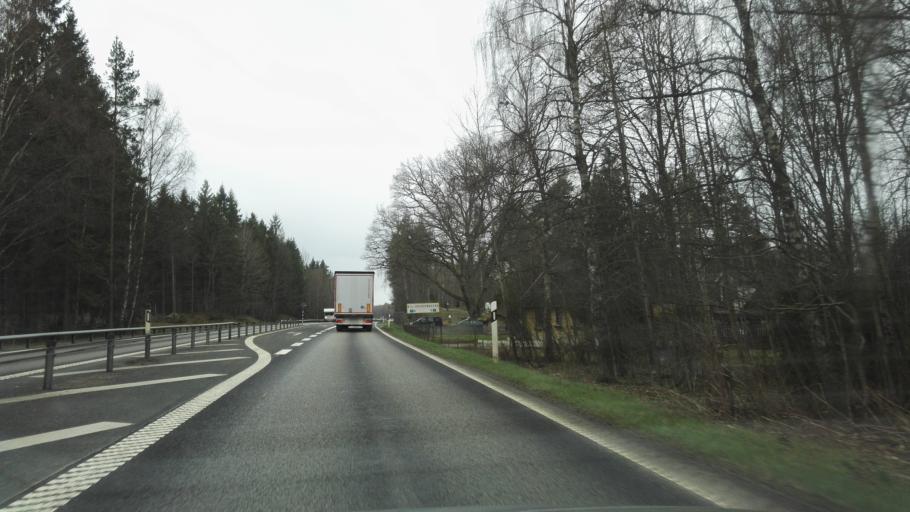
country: SE
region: Skane
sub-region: Osby Kommun
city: Osby
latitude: 56.3412
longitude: 14.0117
